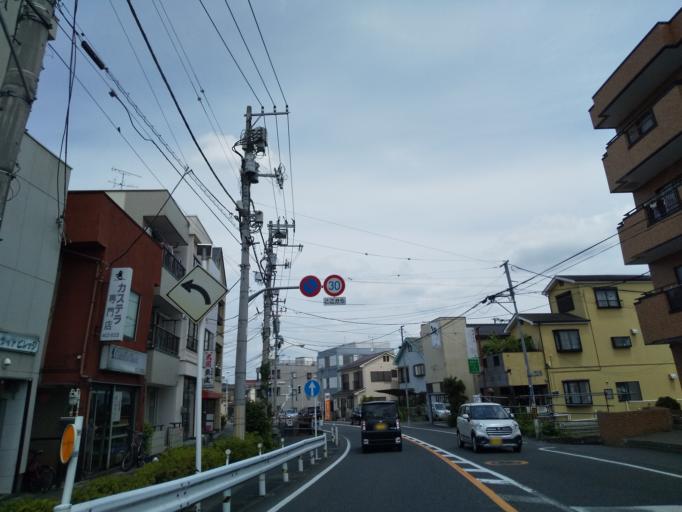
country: JP
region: Tokyo
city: Hachioji
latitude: 35.6670
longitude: 139.3232
